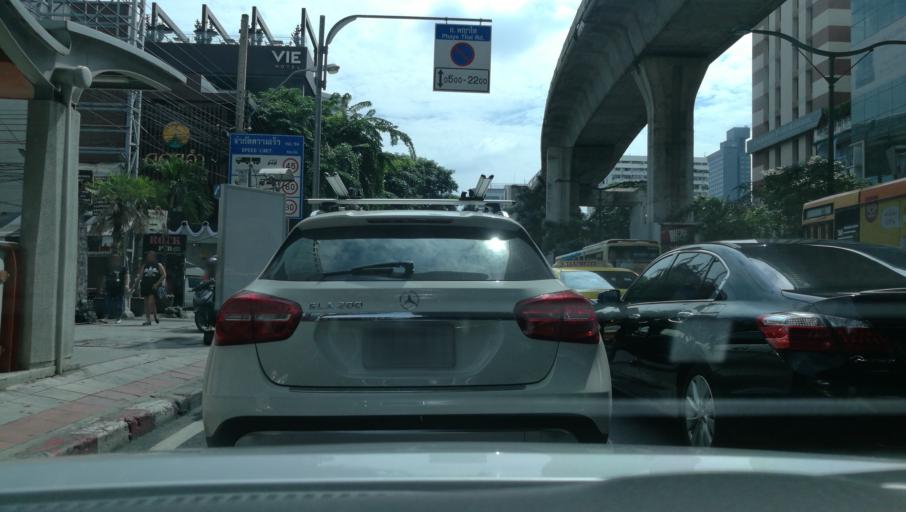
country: TH
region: Bangkok
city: Ratchathewi
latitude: 13.7512
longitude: 100.5317
